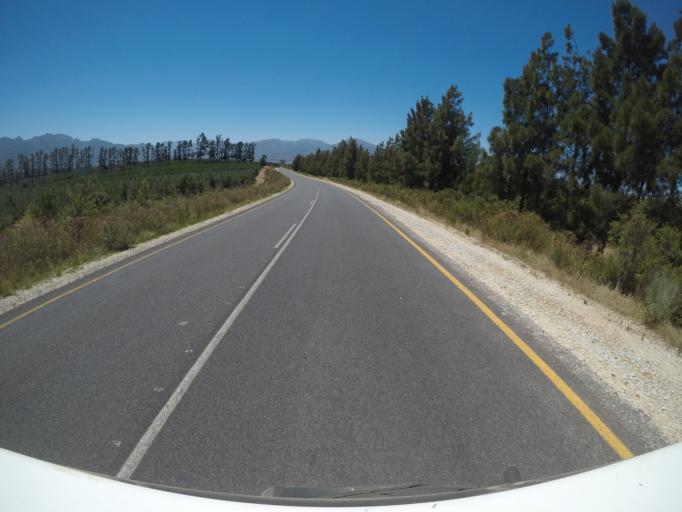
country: ZA
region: Western Cape
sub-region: Overberg District Municipality
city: Grabouw
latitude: -34.0662
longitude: 19.1322
